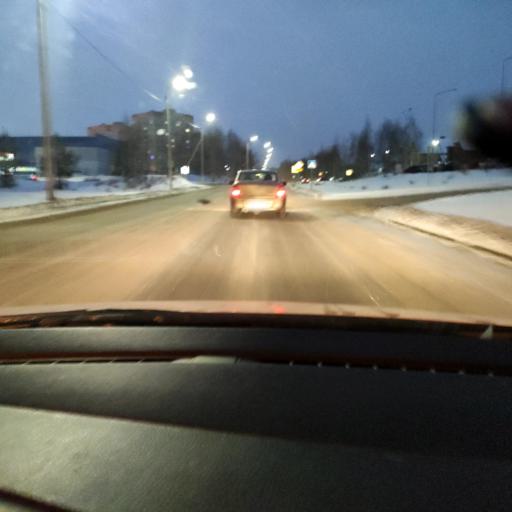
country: RU
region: Tatarstan
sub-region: Zelenodol'skiy Rayon
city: Zelenodolsk
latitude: 55.8659
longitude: 48.5624
